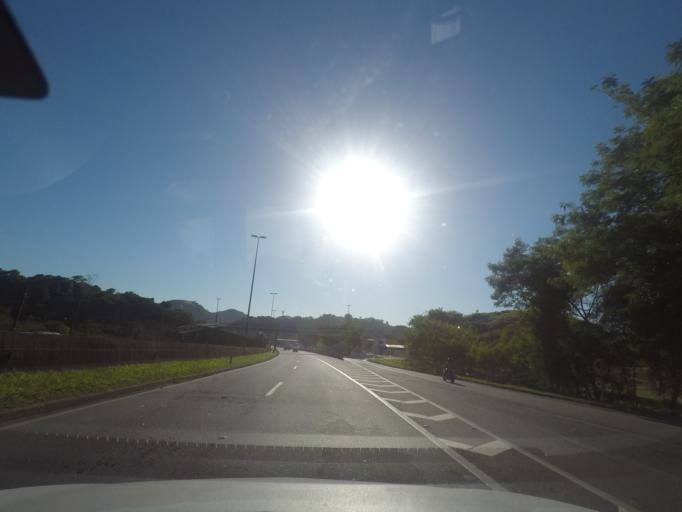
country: BR
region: Rio de Janeiro
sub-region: Petropolis
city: Petropolis
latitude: -22.6573
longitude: -43.1331
